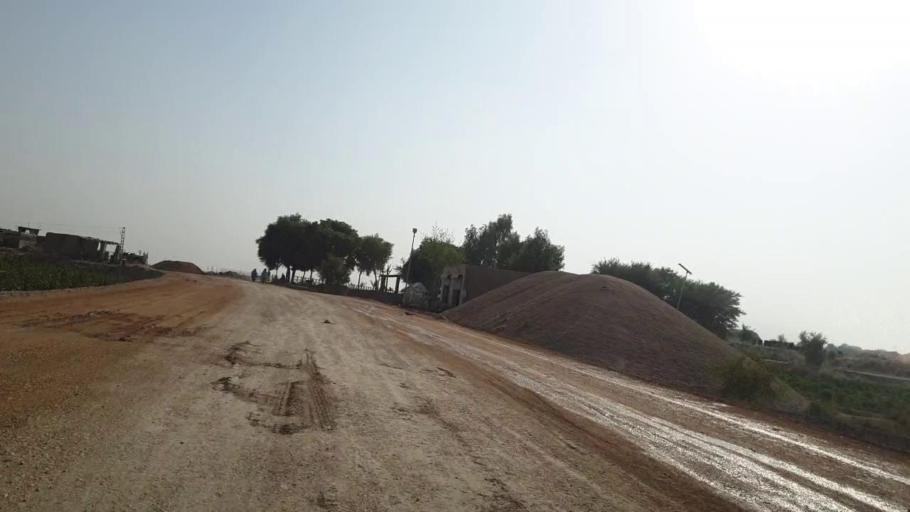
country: PK
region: Sindh
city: Bhan
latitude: 26.5022
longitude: 67.7823
